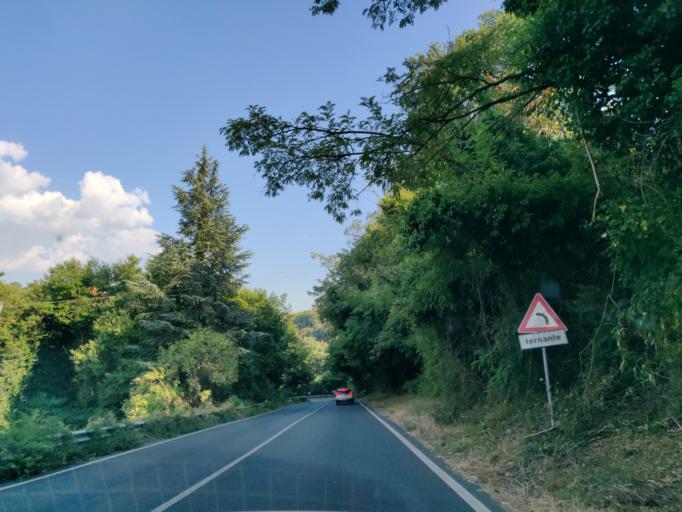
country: IT
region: Latium
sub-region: Provincia di Viterbo
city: Acquapendente
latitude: 42.7506
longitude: 11.8636
